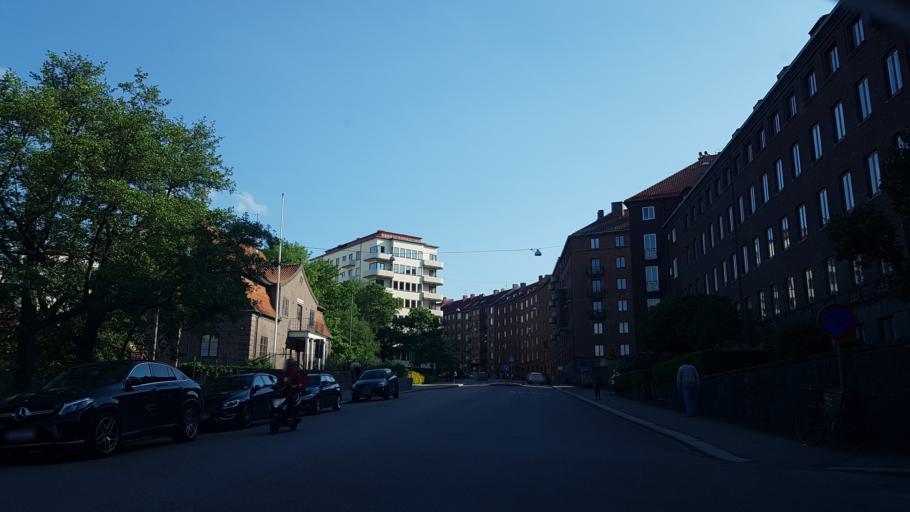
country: SE
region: Vaestra Goetaland
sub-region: Goteborg
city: Goeteborg
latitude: 57.6945
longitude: 11.9796
